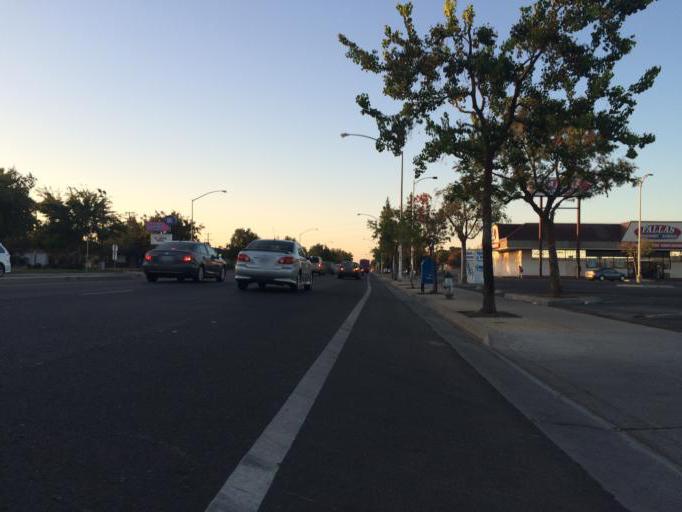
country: US
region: California
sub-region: Fresno County
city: Fresno
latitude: 36.7786
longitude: -119.7545
